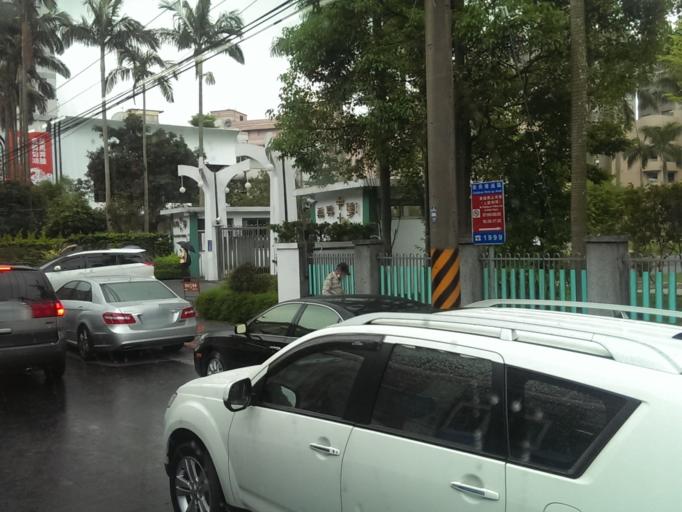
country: TW
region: Taipei
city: Taipei
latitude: 24.9906
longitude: 121.5589
